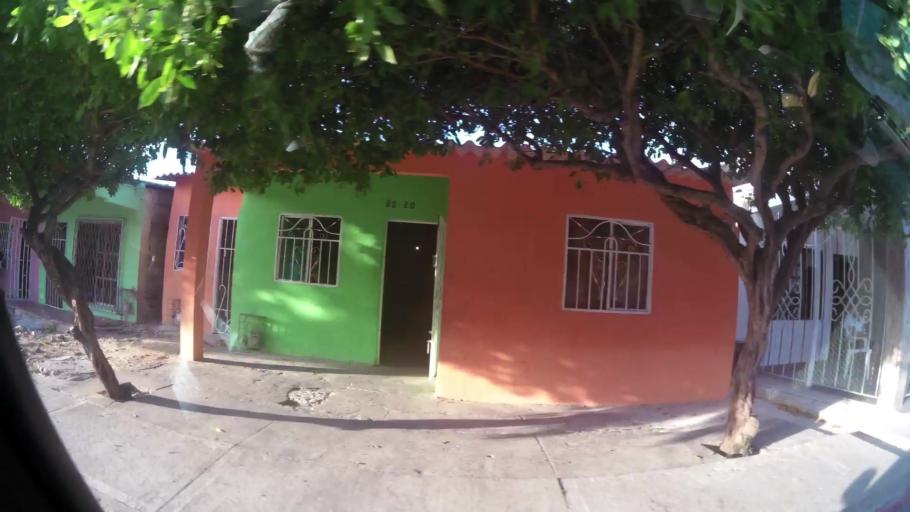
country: CO
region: Atlantico
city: Barranquilla
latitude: 10.9566
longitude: -74.8228
